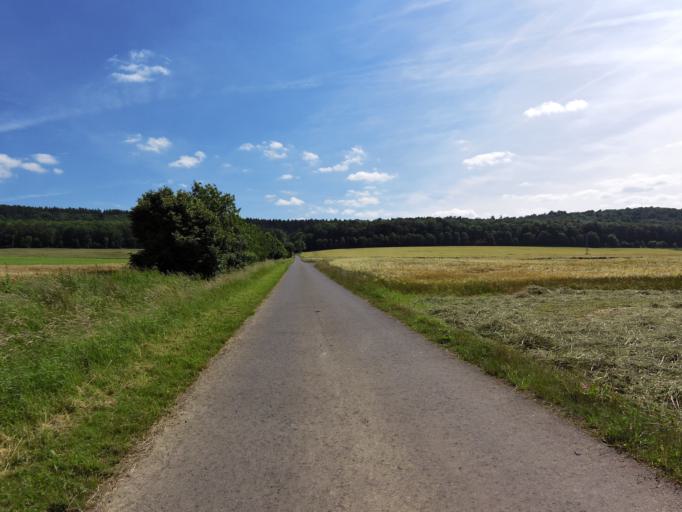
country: DE
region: Thuringia
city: Seebach
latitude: 50.9738
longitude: 10.4334
